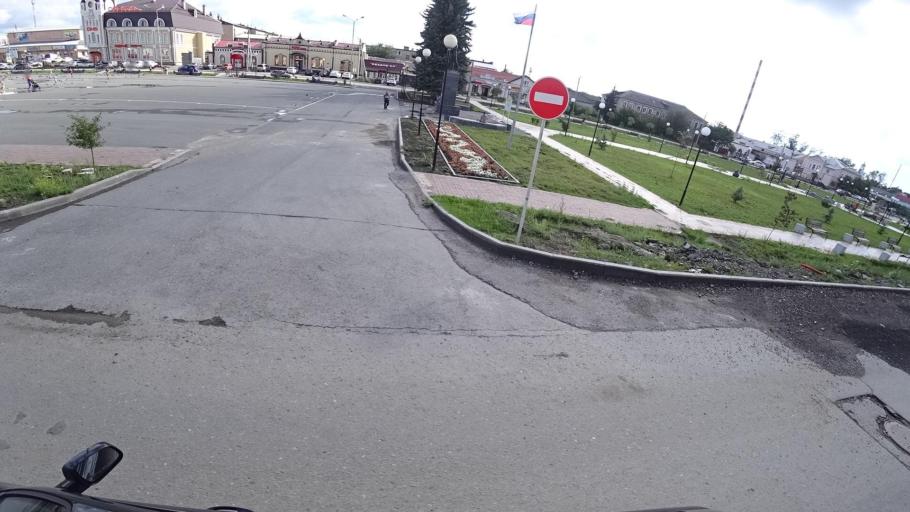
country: RU
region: Sverdlovsk
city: Kamyshlov
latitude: 56.8445
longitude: 62.7074
